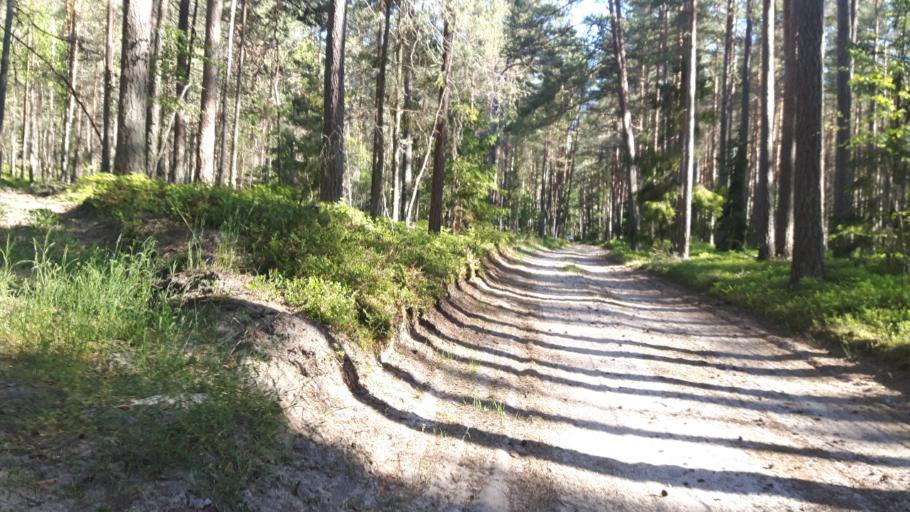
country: LV
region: Salacgrivas
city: Salacgriva
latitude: 57.7116
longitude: 24.3515
